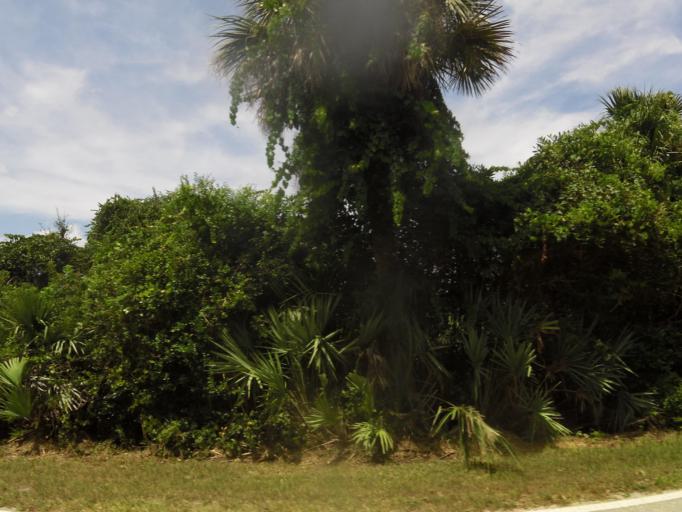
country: US
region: Florida
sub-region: Volusia County
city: Ponce Inlet
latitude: 29.0836
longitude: -80.9297
